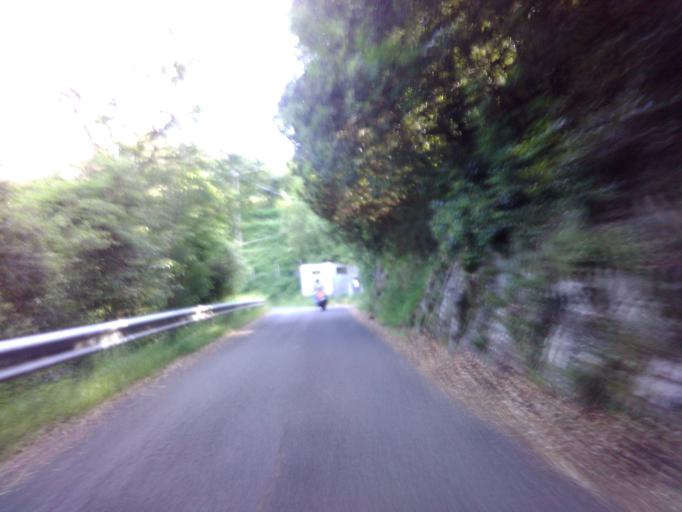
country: IT
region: Tuscany
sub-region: Provincia di Massa-Carrara
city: Fosdinovo
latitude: 44.1605
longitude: 9.9983
